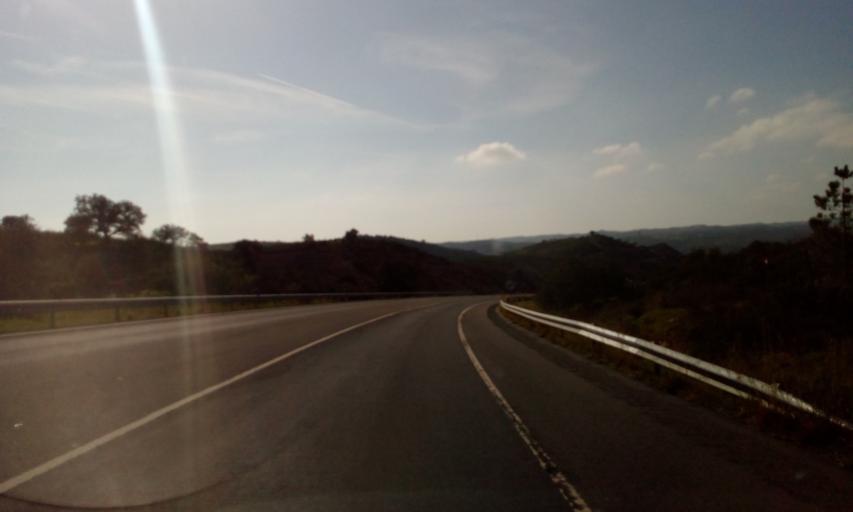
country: PT
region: Faro
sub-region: Castro Marim
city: Castro Marim
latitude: 37.2856
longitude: -7.4865
